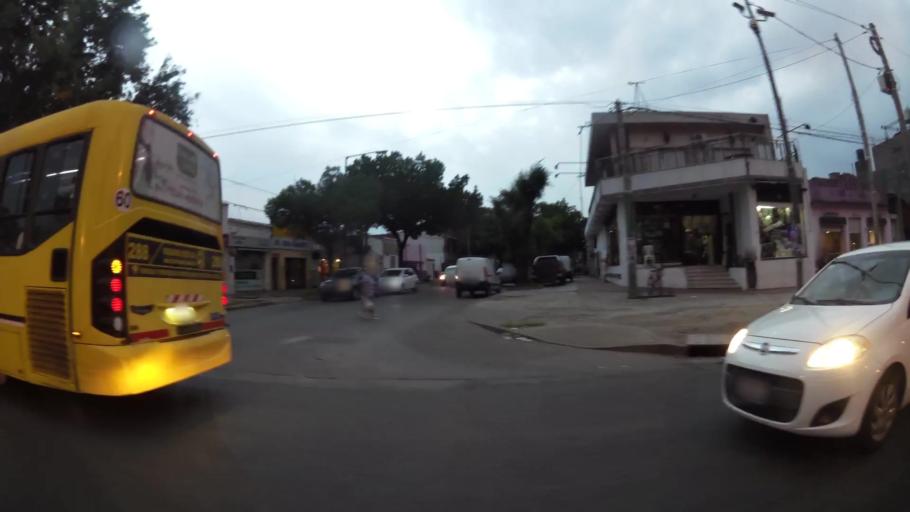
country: AR
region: Santa Fe
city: Granadero Baigorria
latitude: -32.8844
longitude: -60.6957
